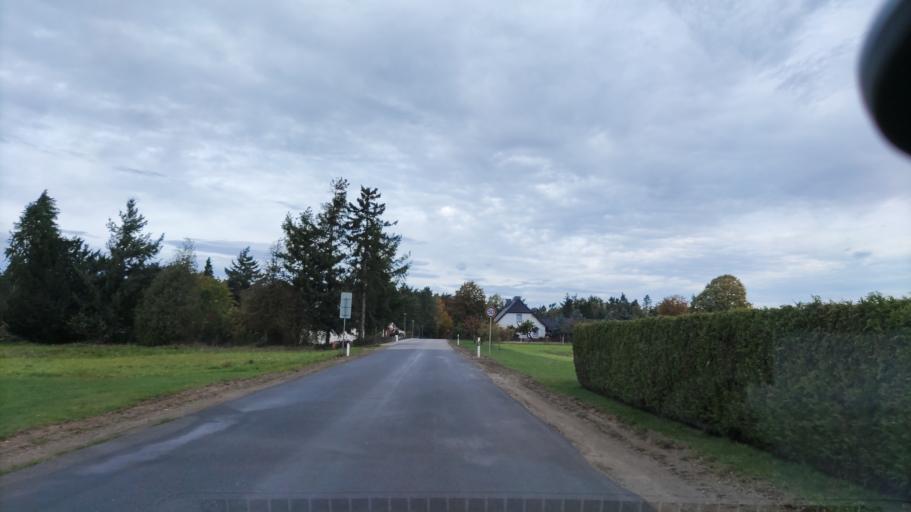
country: DE
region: Mecklenburg-Vorpommern
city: Boizenburg
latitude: 53.3695
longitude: 10.8604
